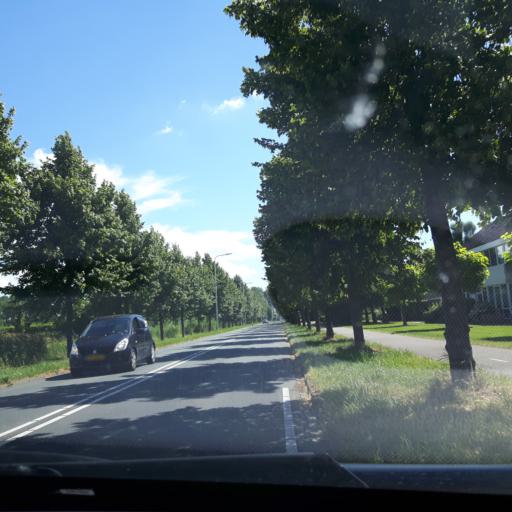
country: NL
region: Zeeland
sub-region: Gemeente Goes
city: Goes
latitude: 51.5065
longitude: 3.9071
